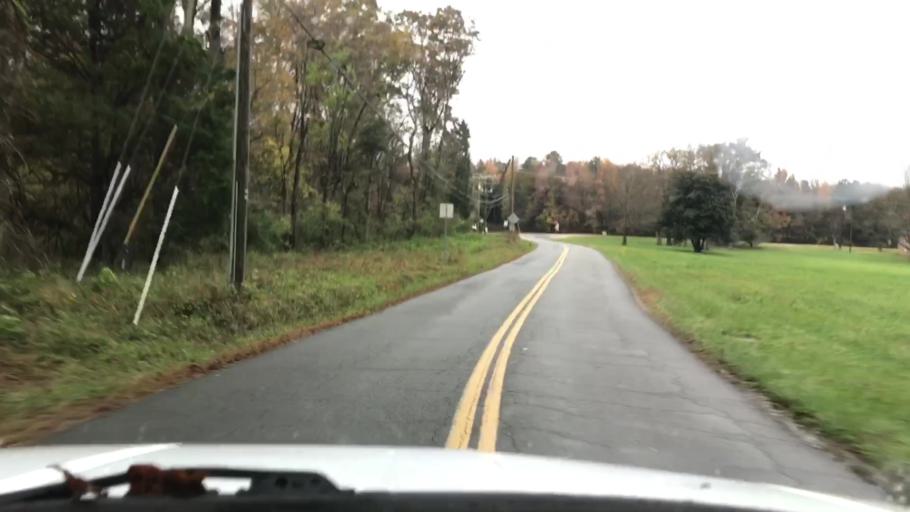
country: US
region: Virginia
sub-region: Henrico County
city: Short Pump
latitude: 37.6036
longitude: -77.7021
